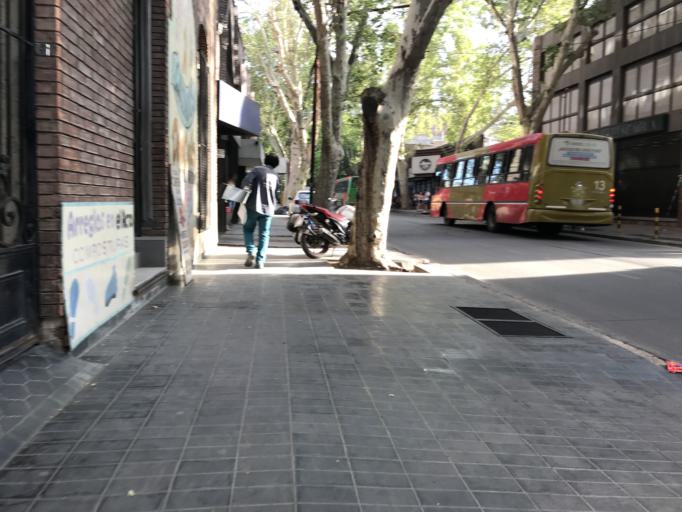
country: AR
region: Mendoza
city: Mendoza
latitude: -32.8900
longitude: -68.8355
